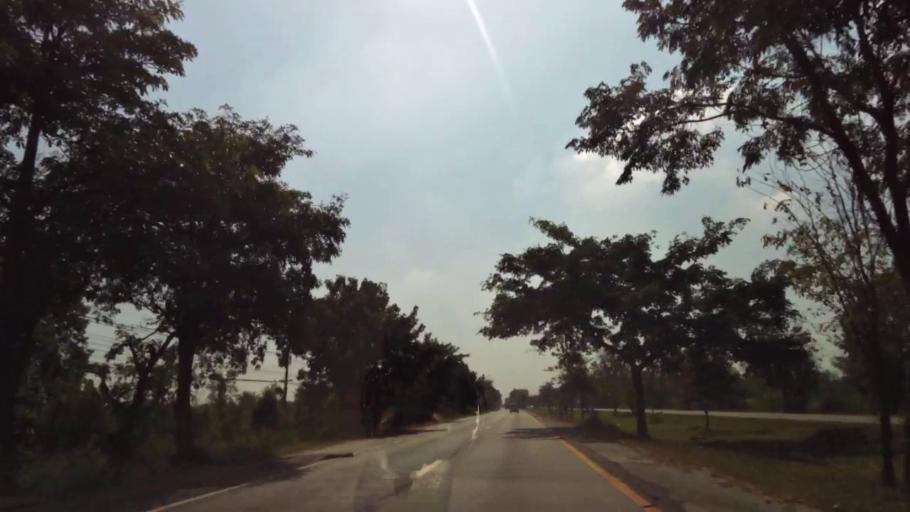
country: TH
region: Phichit
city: Wachira Barami
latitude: 16.5381
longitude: 100.1445
